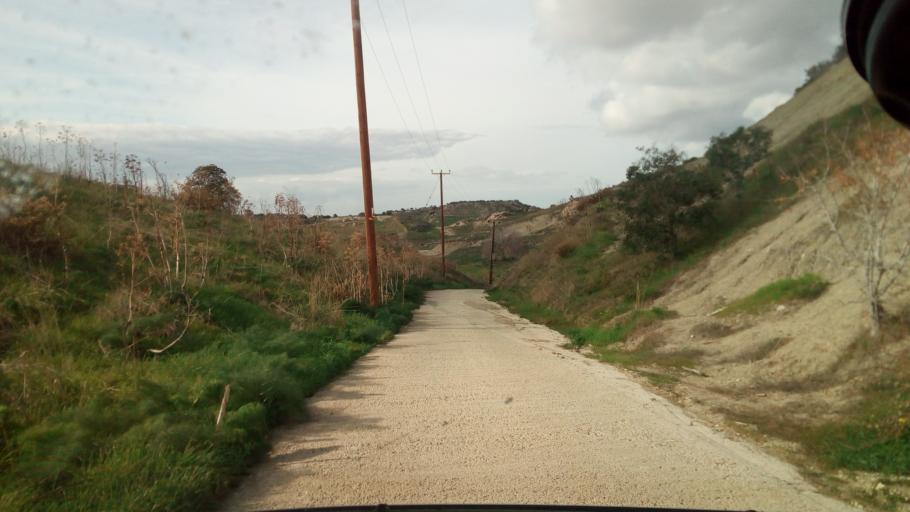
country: CY
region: Pafos
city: Mesogi
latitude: 34.7949
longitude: 32.4774
